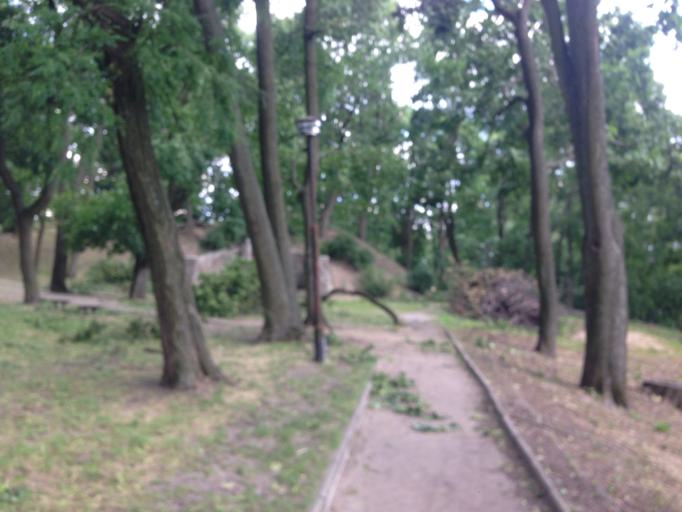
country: PL
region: Warmian-Masurian Voivodeship
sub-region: Powiat nidzicki
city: Nidzica
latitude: 53.3592
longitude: 20.4290
